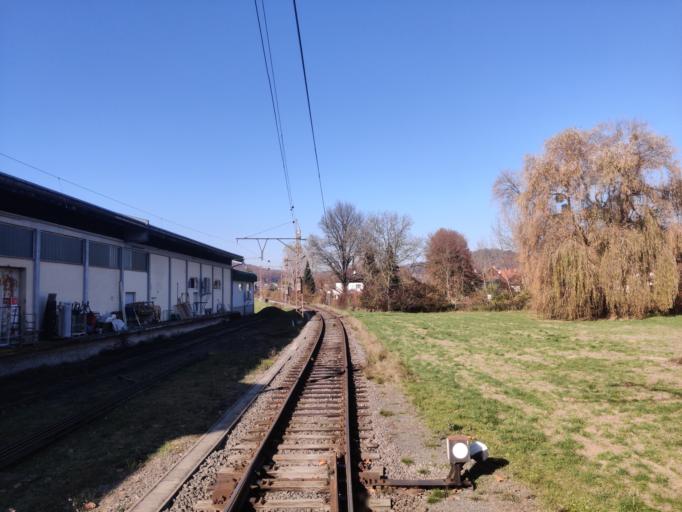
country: AT
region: Styria
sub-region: Politischer Bezirk Suedoststeiermark
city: Bad Gleichenberg
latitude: 46.8729
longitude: 15.9023
